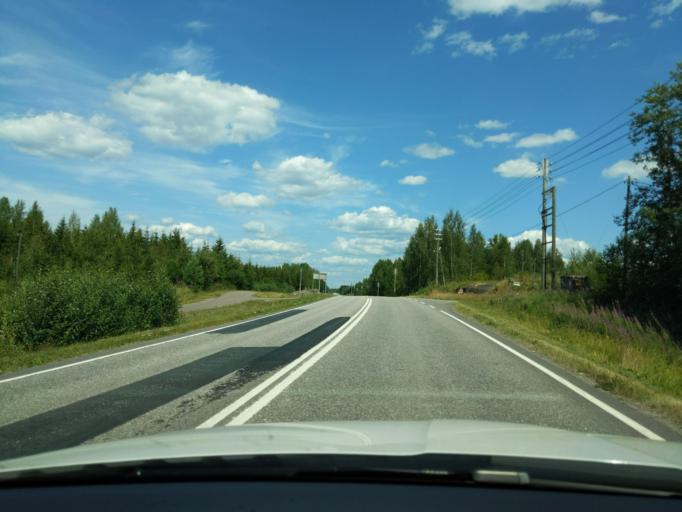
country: FI
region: Paijanne Tavastia
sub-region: Lahti
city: Heinola
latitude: 61.1136
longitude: 25.9451
